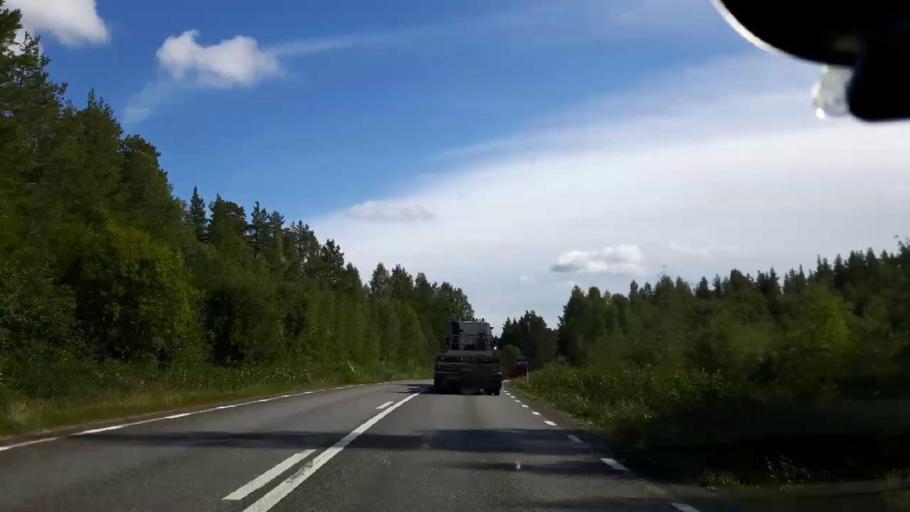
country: SE
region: Jaemtland
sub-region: Braecke Kommun
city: Braecke
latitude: 63.1943
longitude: 15.4154
